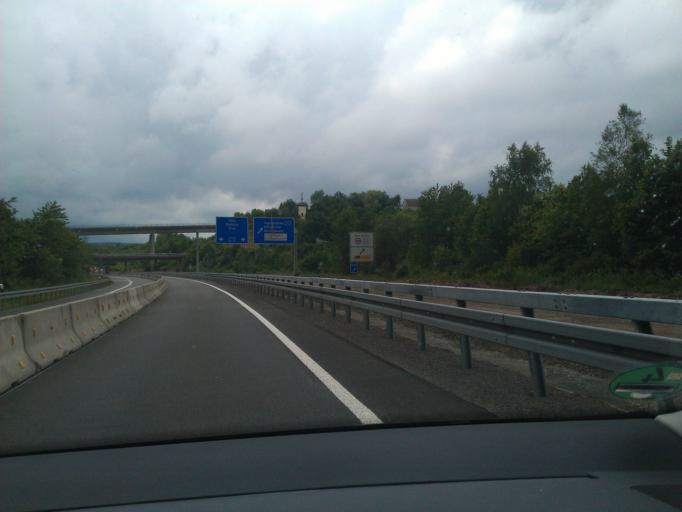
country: DE
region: Rheinland-Pfalz
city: Neuhutten
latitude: 49.5962
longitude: 6.9979
